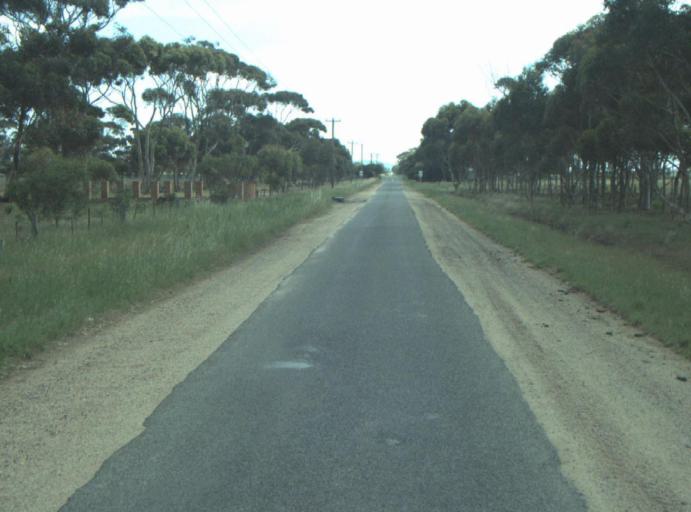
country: AU
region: Victoria
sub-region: Greater Geelong
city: Lara
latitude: -38.0596
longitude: 144.4269
